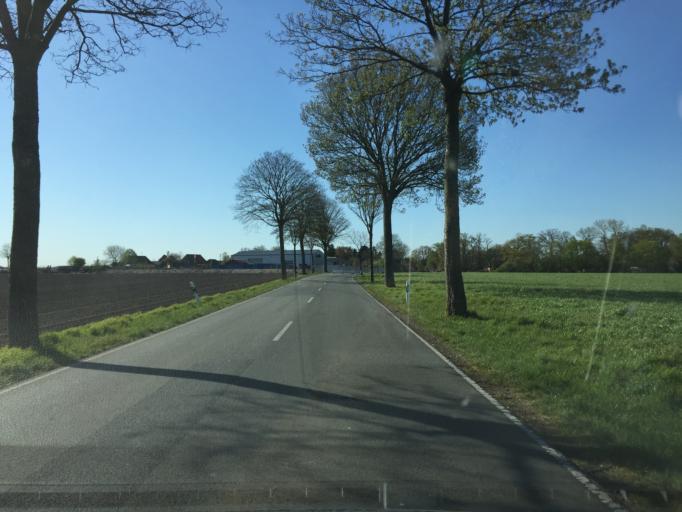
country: DE
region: Lower Saxony
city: Varrel
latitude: 52.6277
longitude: 8.7392
